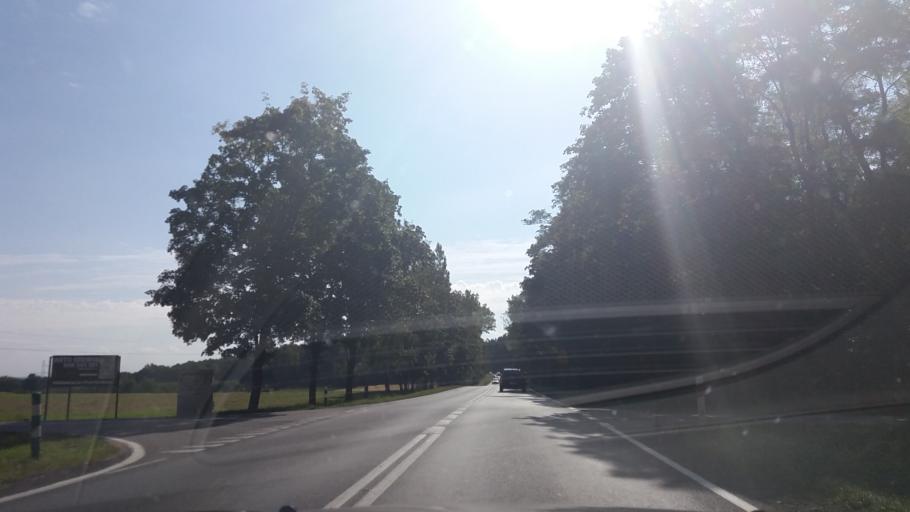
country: PL
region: Lower Silesian Voivodeship
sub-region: Powiat legnicki
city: Prochowice
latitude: 51.3030
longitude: 16.3349
